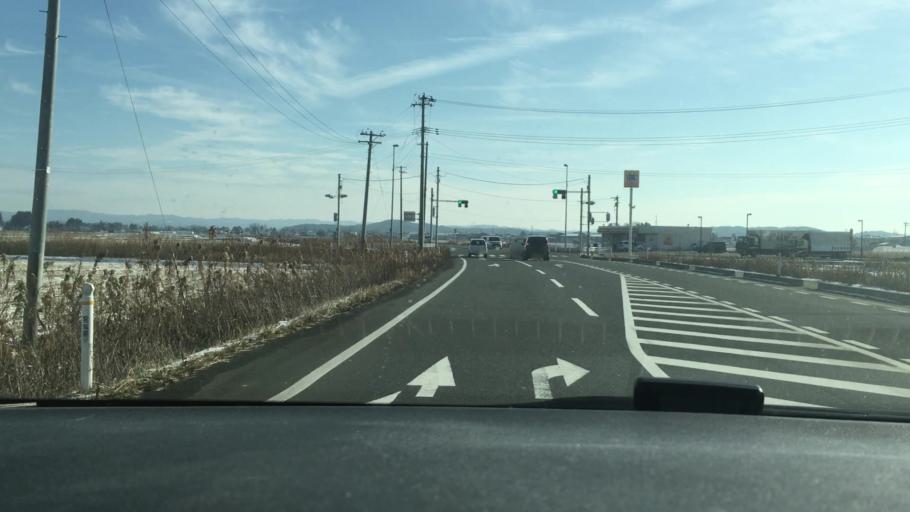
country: JP
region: Iwate
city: Ichinoseki
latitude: 38.7773
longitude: 141.1313
